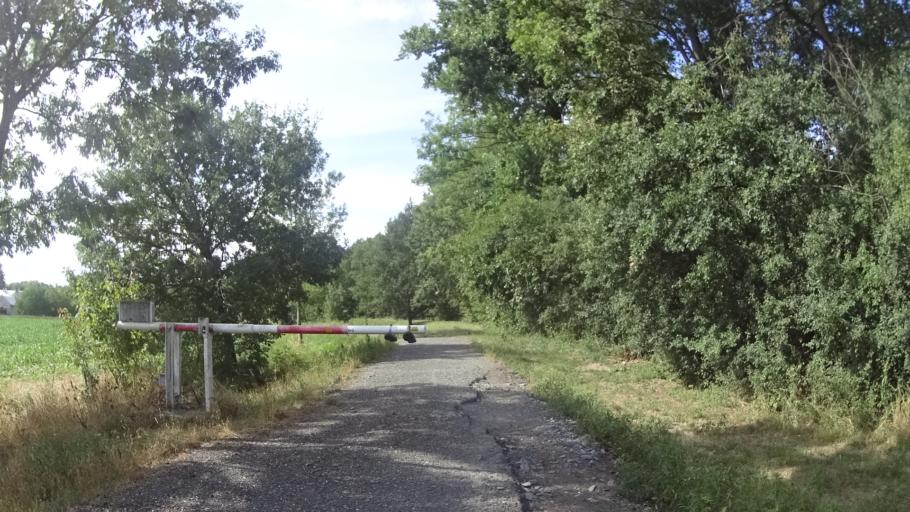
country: CZ
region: Olomoucky
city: Naklo
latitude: 49.6781
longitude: 17.1484
